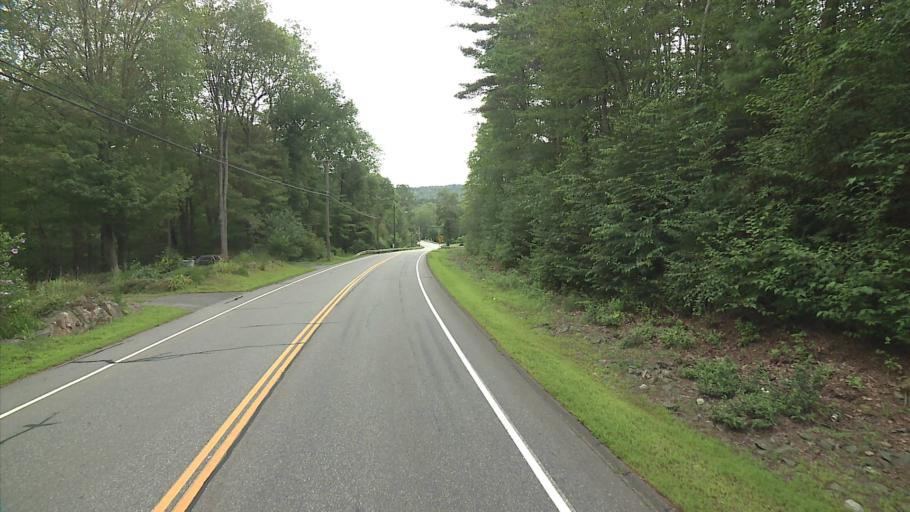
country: US
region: Connecticut
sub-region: Tolland County
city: Storrs
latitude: 41.8741
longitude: -72.2453
